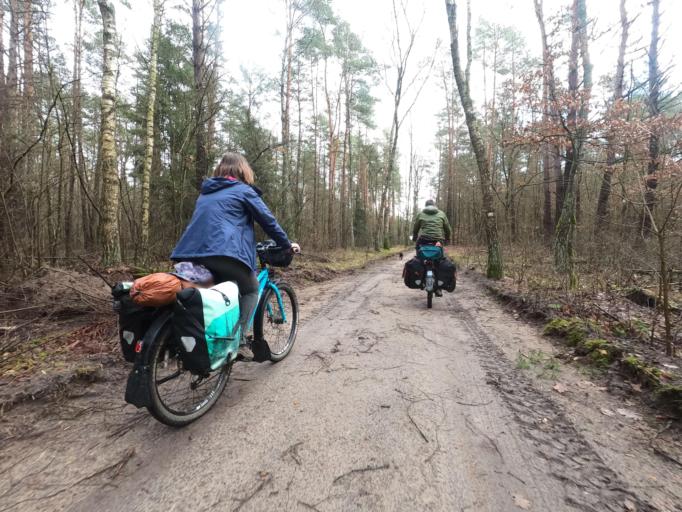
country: PL
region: Greater Poland Voivodeship
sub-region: Powiat pilski
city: Smilowo
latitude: 53.1126
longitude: 16.9322
